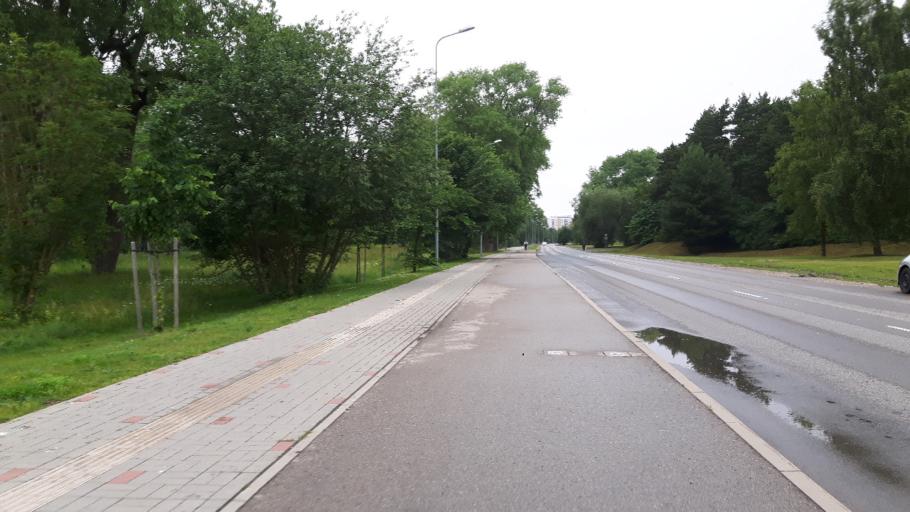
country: LV
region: Liepaja
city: Liepaja
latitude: 56.4804
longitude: 21.0076
